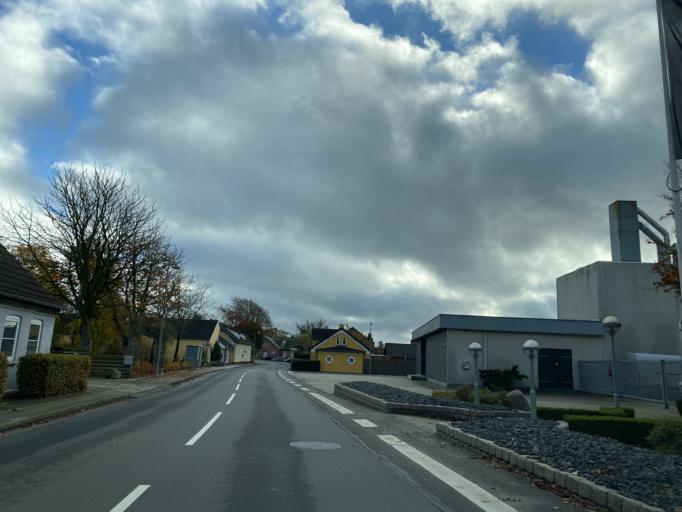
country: DK
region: Central Jutland
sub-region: Favrskov Kommune
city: Hammel
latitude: 56.2429
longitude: 9.8146
